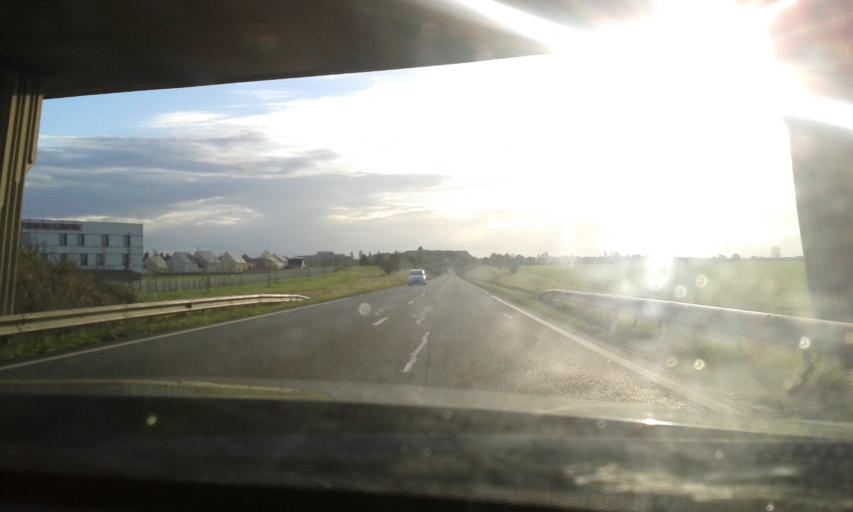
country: FR
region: Centre
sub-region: Departement d'Eure-et-Loir
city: Mainvilliers
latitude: 48.4617
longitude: 1.4555
